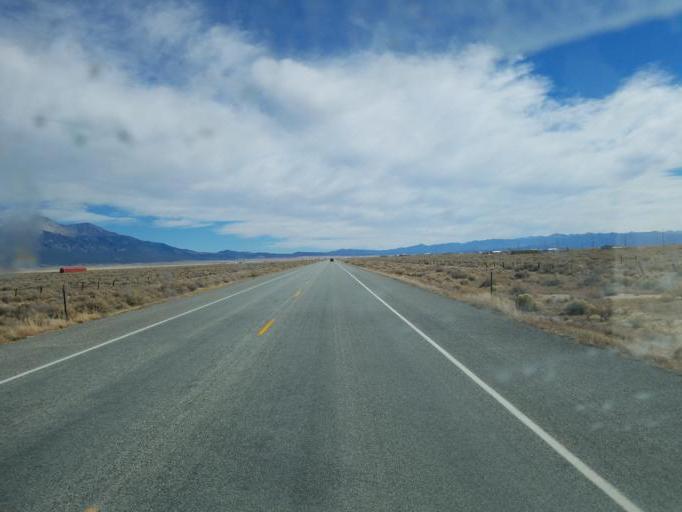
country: US
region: Colorado
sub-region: Alamosa County
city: Alamosa East
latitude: 37.4749
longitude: -105.7068
